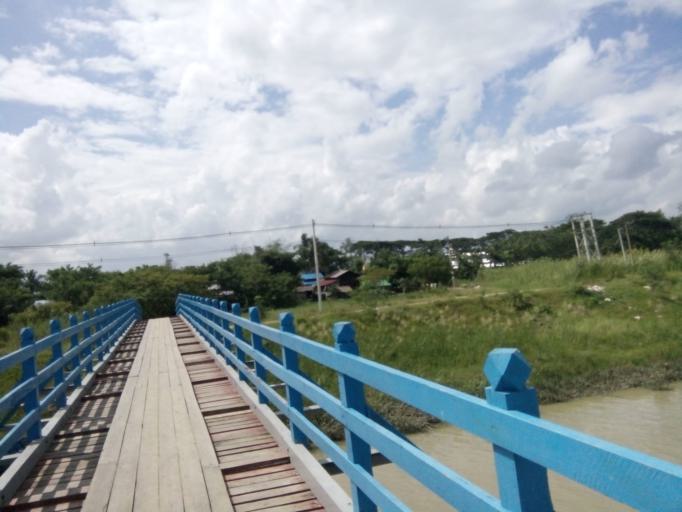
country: MM
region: Yangon
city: Kanbe
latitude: 16.8711
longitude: 95.9814
